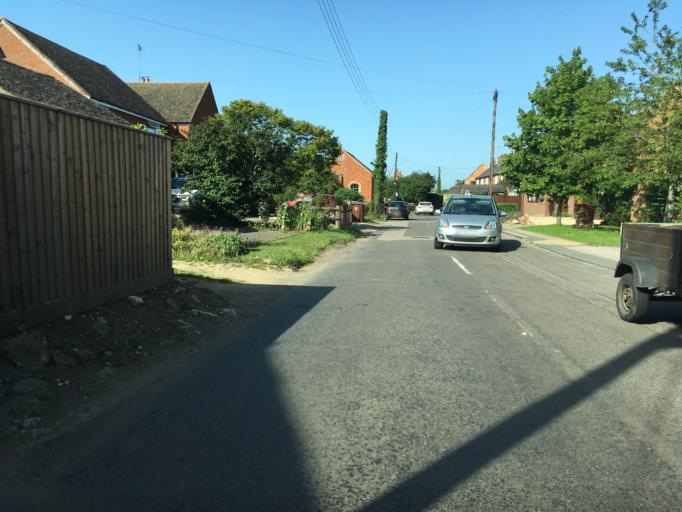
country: GB
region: England
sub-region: Buckinghamshire
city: Steeple Claydon
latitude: 51.9308
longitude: -1.0374
